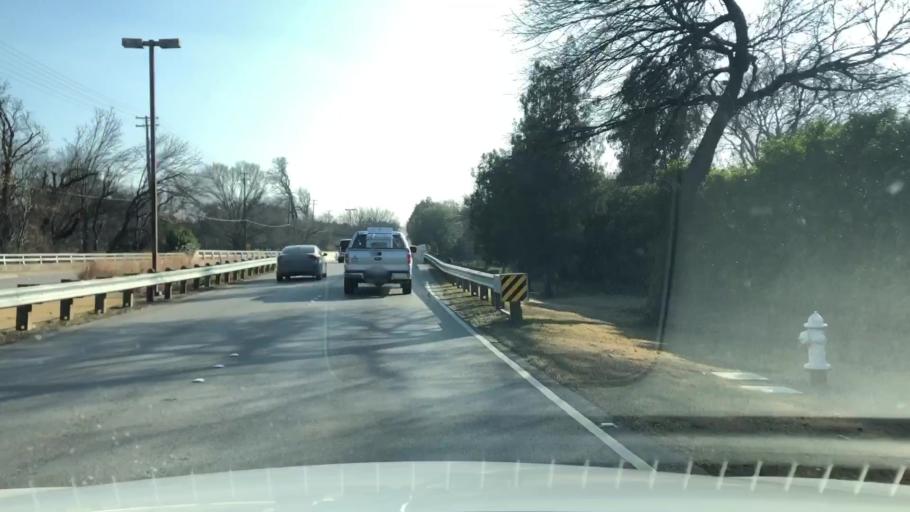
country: US
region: Texas
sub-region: Dallas County
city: Farmers Branch
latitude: 32.9310
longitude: -96.8557
